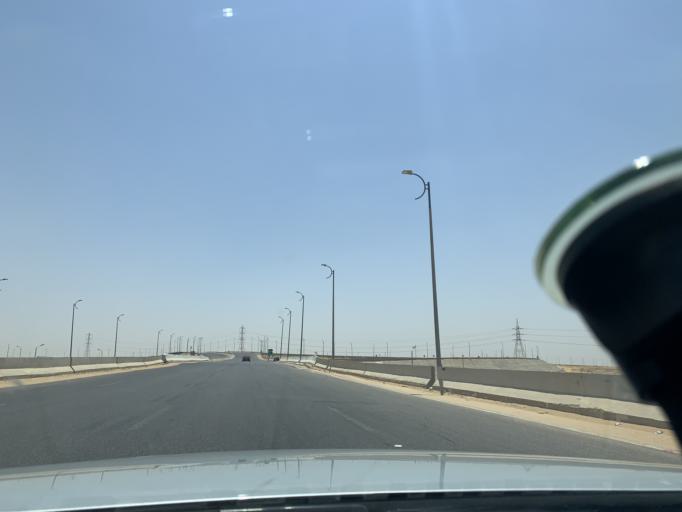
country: EG
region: Muhafazat al Qahirah
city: Halwan
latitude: 29.9716
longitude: 31.4697
